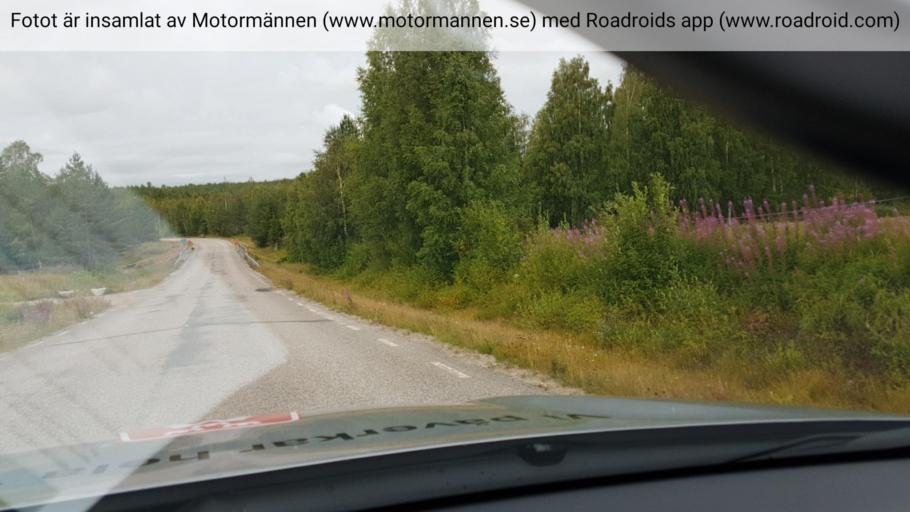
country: SE
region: Norrbotten
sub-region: Bodens Kommun
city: Saevast
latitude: 65.6666
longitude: 21.6739
